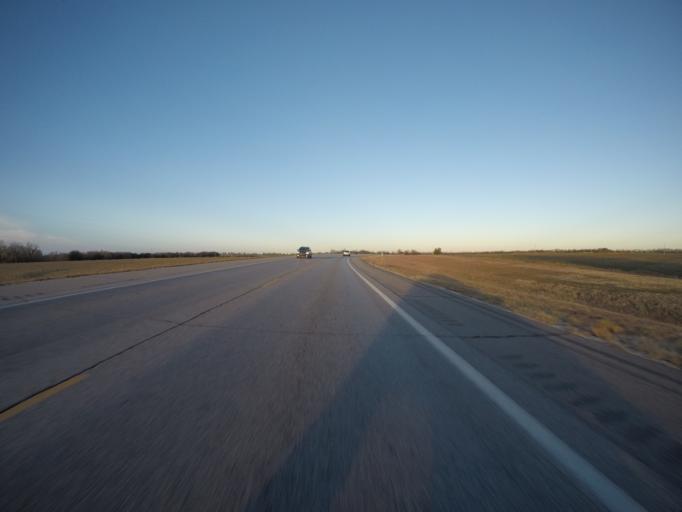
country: US
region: Kansas
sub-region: Marion County
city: Peabody
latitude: 38.1723
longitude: -97.1932
